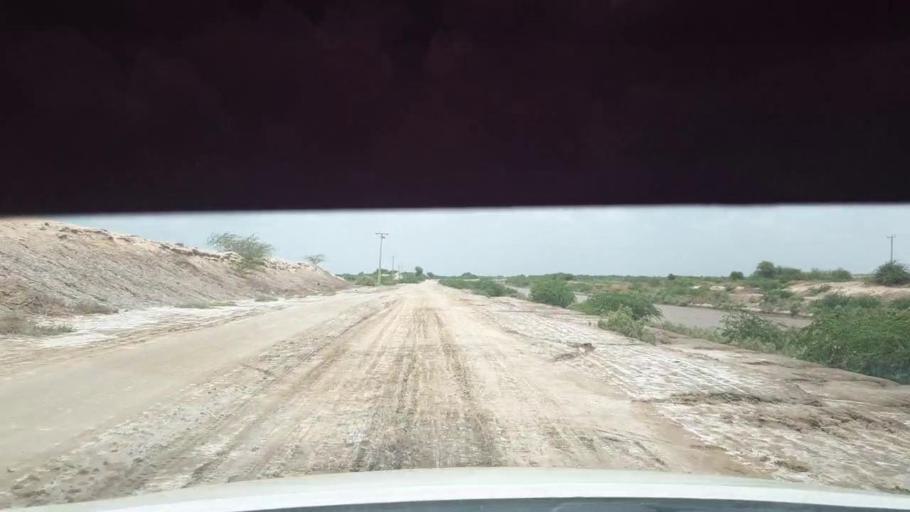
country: PK
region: Sindh
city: Kadhan
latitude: 24.5196
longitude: 69.1215
